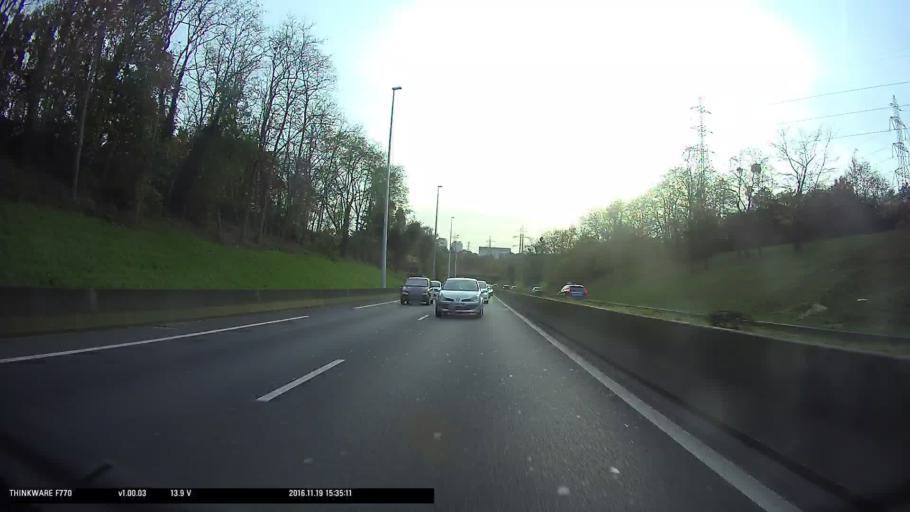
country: FR
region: Ile-de-France
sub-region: Departement du Val-d'Oise
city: Pontoise
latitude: 49.0588
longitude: 2.0832
